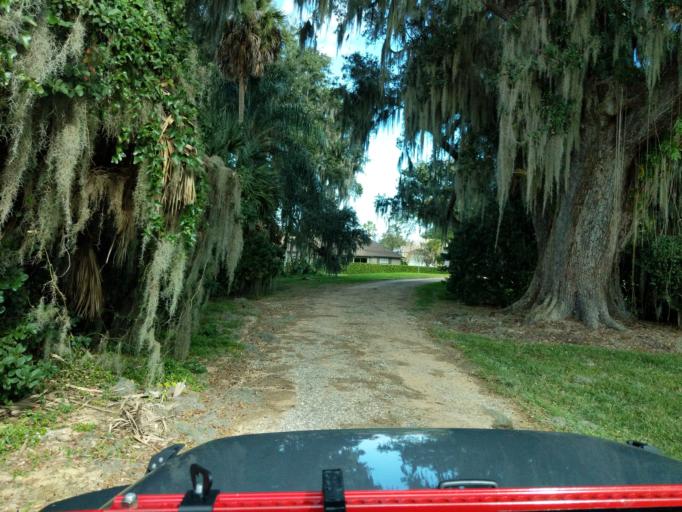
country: US
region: Florida
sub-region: Orange County
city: Oakland
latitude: 28.5599
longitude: -81.6305
